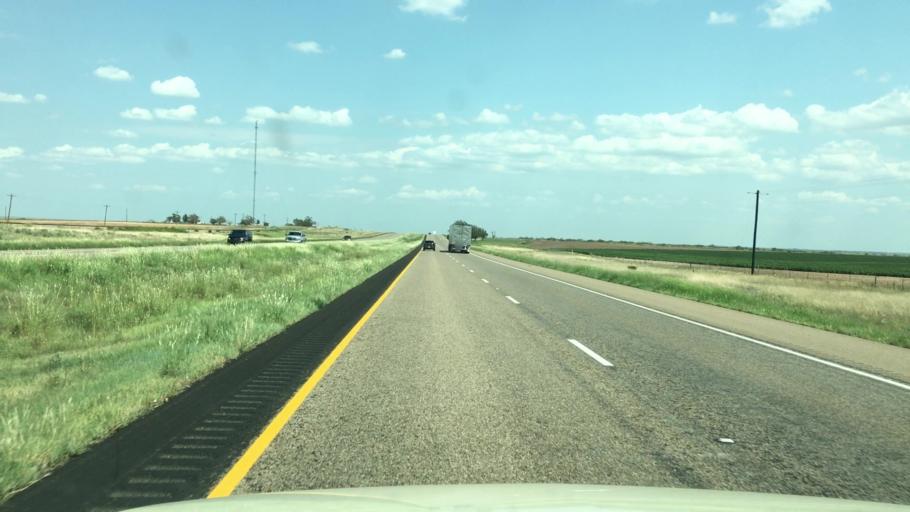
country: US
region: Texas
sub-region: Armstrong County
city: Claude
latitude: 35.0330
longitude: -101.1577
